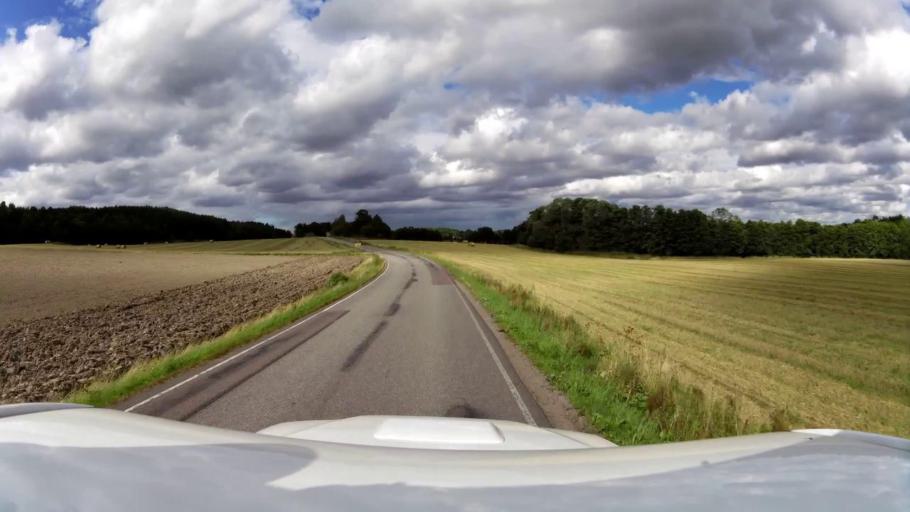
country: SE
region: OEstergoetland
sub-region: Linkopings Kommun
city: Sturefors
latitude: 58.3158
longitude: 15.7224
